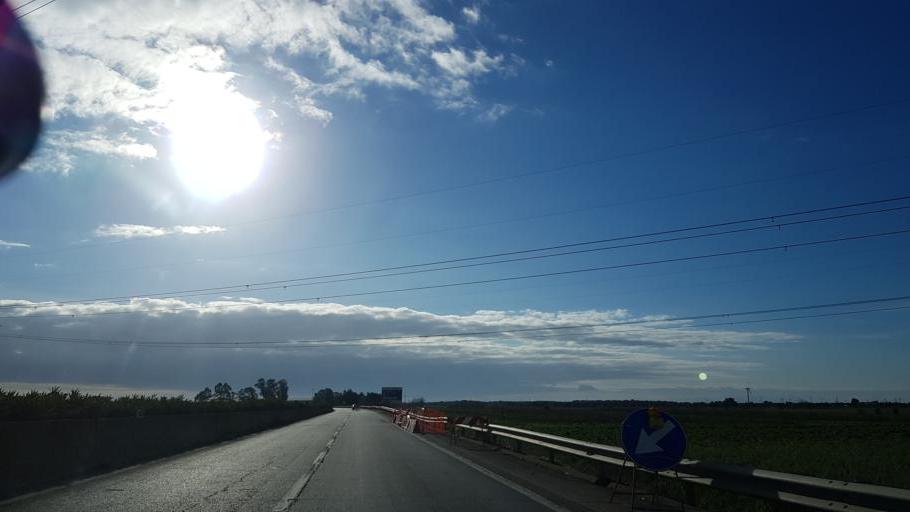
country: IT
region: Apulia
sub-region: Provincia di Brindisi
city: Tuturano
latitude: 40.5605
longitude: 17.9898
